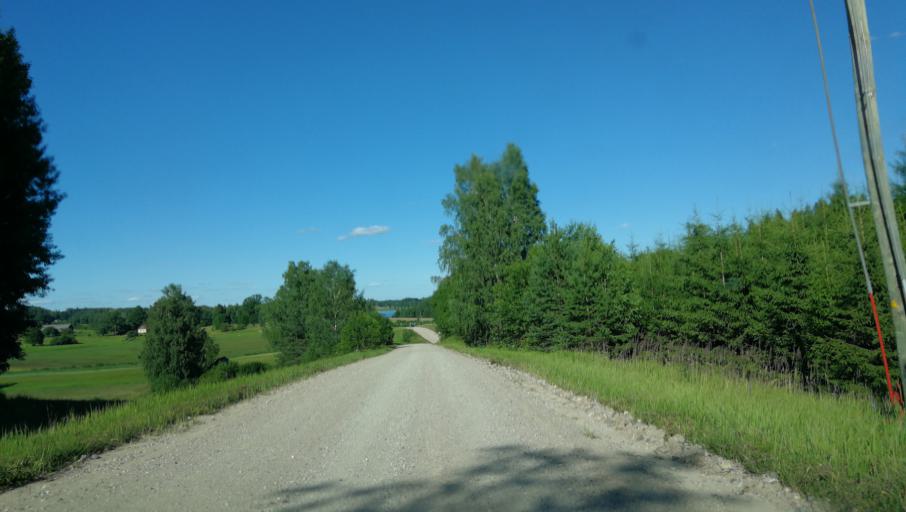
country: LV
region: Jaunpiebalga
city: Jaunpiebalga
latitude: 56.9959
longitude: 26.0242
